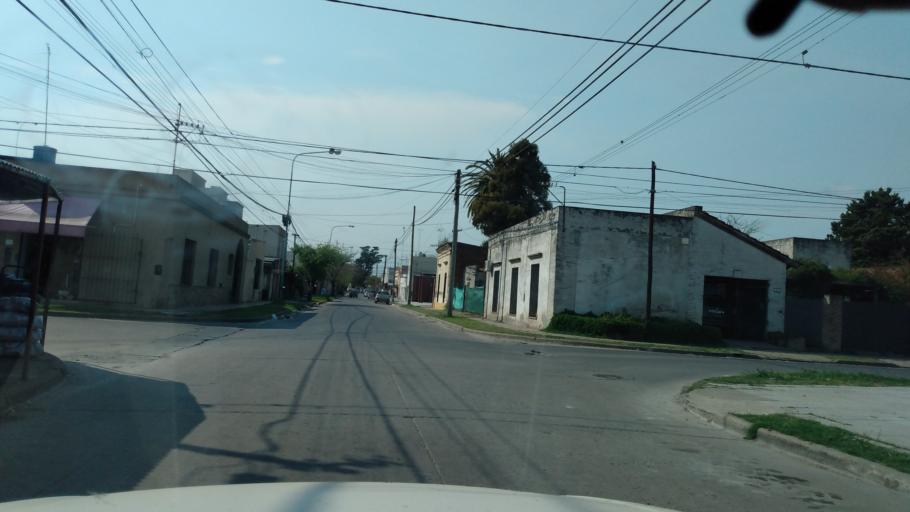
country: AR
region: Buenos Aires
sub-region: Partido de Lujan
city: Lujan
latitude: -34.5729
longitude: -59.1172
